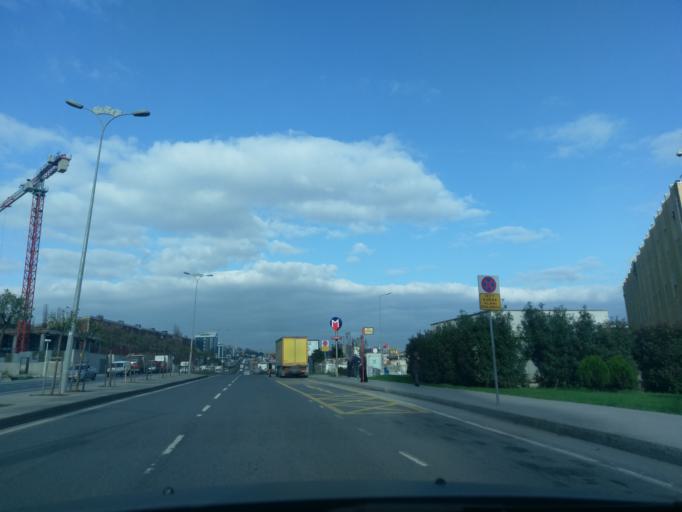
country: TR
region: Istanbul
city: Basaksehir
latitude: 41.0700
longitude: 28.8050
